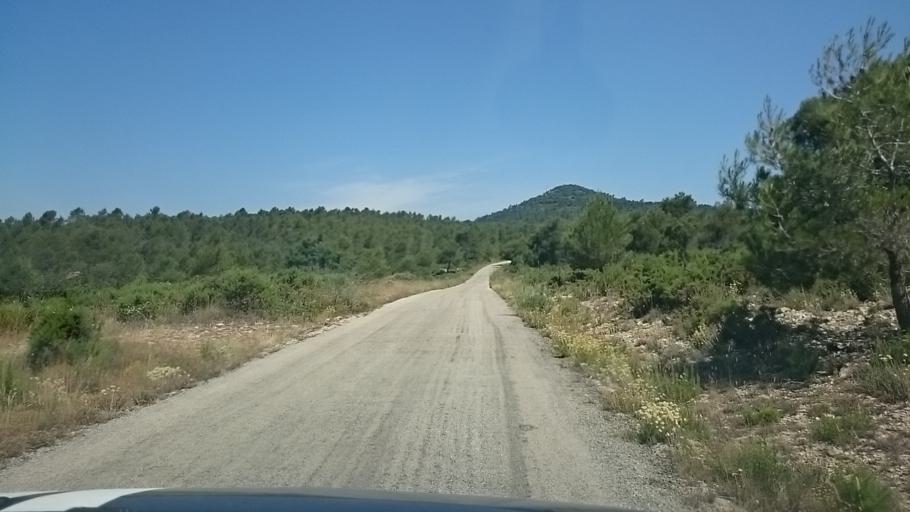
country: ES
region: Catalonia
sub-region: Provincia de Tarragona
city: Querol
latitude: 41.3932
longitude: 1.4277
